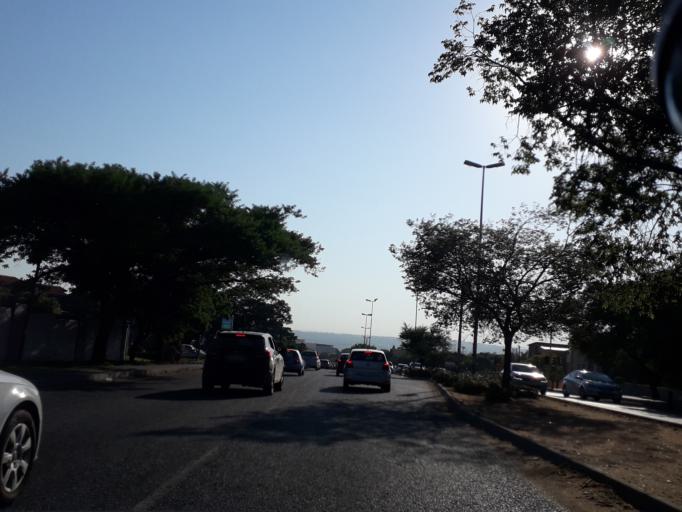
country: ZA
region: Gauteng
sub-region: West Rand District Municipality
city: Muldersdriseloop
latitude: -26.0623
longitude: 27.9506
